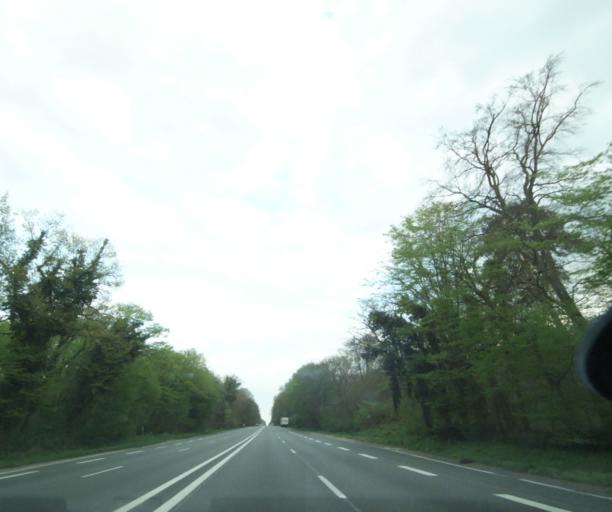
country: FR
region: Ile-de-France
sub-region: Departement de Seine-et-Marne
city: Fontainebleau
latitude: 48.4282
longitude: 2.6634
